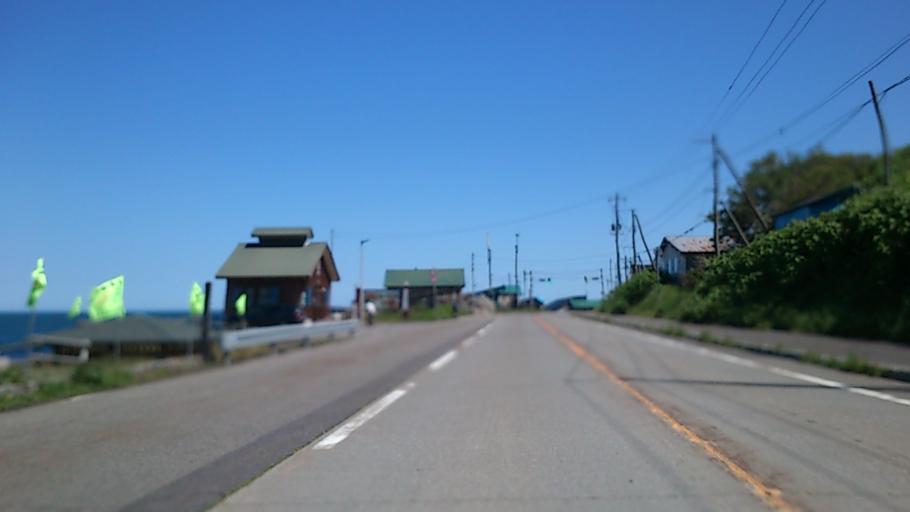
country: JP
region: Hokkaido
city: Rumoi
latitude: 43.7382
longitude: 141.3387
